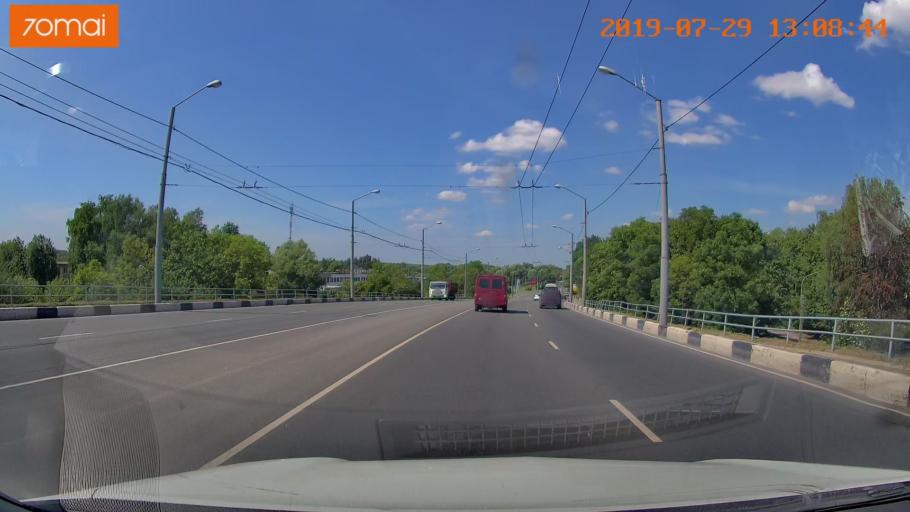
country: RU
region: Kaliningrad
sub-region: Gorod Kaliningrad
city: Kaliningrad
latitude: 54.7121
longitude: 20.4267
